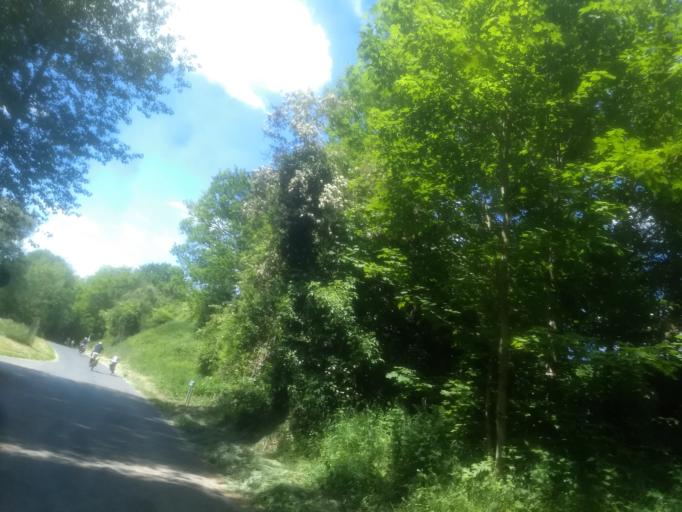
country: FR
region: Nord-Pas-de-Calais
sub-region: Departement du Pas-de-Calais
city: Riviere
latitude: 50.2411
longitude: 2.7080
